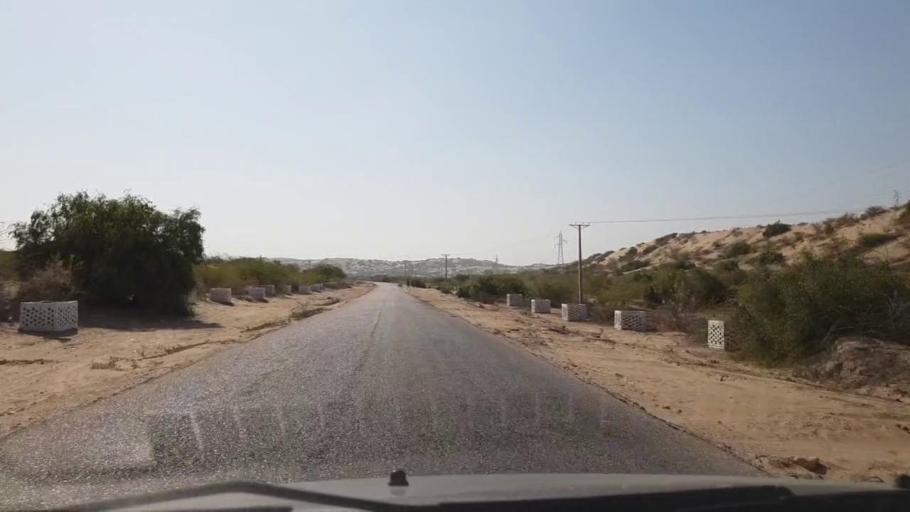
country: PK
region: Sindh
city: Diplo
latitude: 24.4841
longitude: 69.5846
